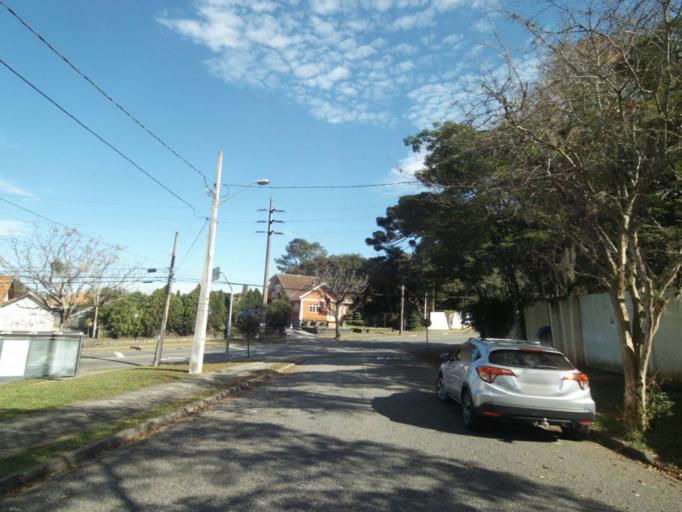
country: BR
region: Parana
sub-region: Curitiba
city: Curitiba
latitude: -25.4027
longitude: -49.2824
